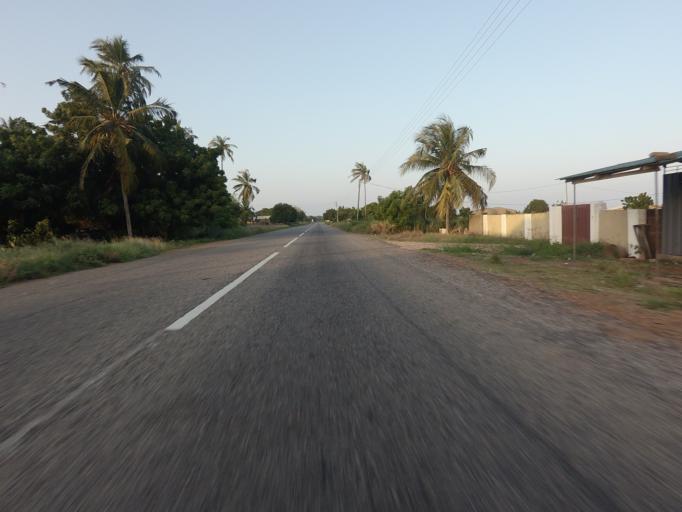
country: GH
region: Volta
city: Anloga
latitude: 5.7858
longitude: 0.8536
